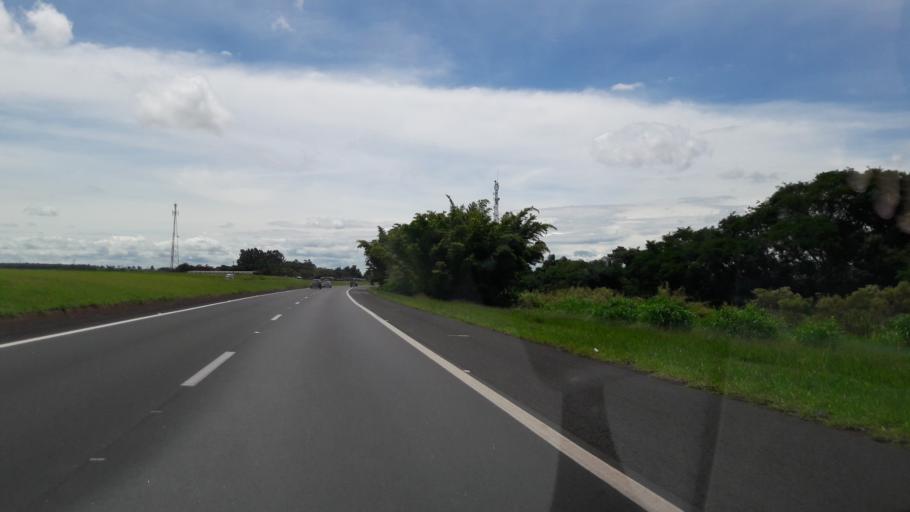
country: BR
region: Sao Paulo
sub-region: Avare
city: Avare
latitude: -22.9573
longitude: -48.8563
